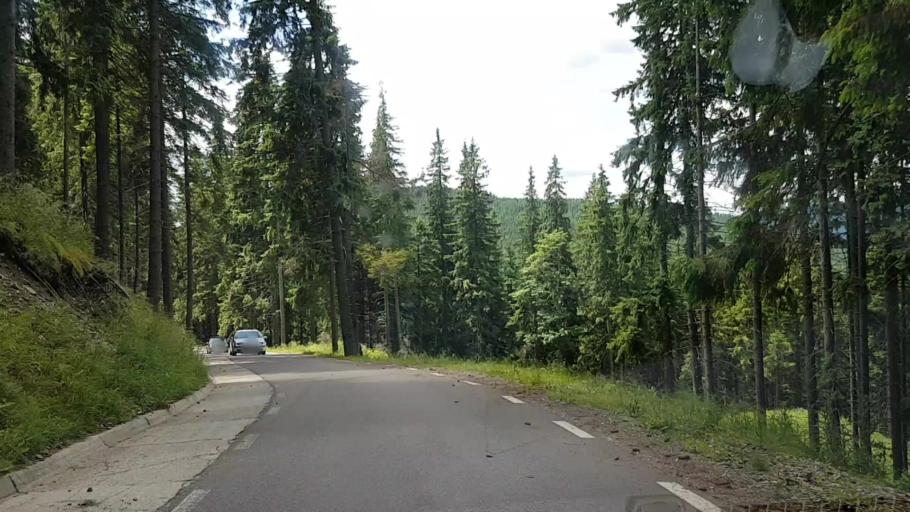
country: RO
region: Suceava
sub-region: Municipiul Campulung Moldovenesc
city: Campulung Moldovenesc
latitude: 47.4410
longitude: 25.5520
